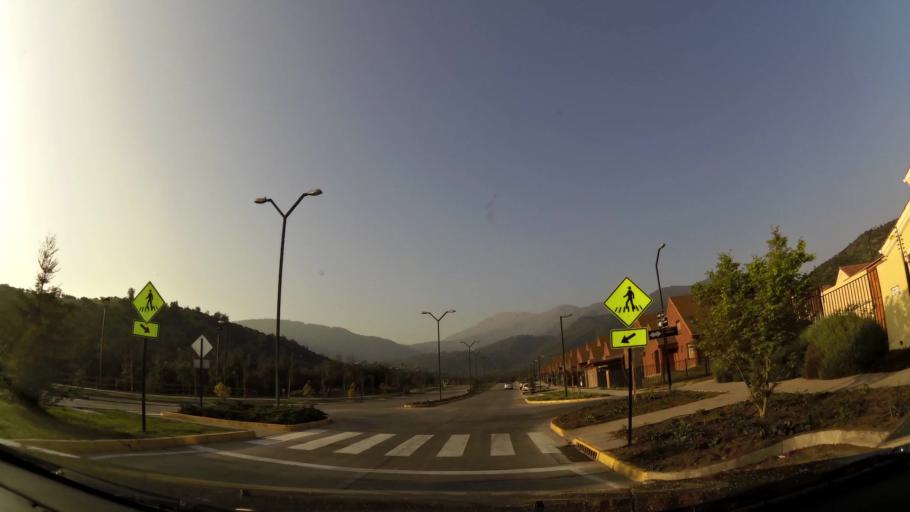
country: CL
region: Santiago Metropolitan
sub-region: Provincia de Santiago
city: Villa Presidente Frei, Nunoa, Santiago, Chile
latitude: -33.3287
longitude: -70.5053
